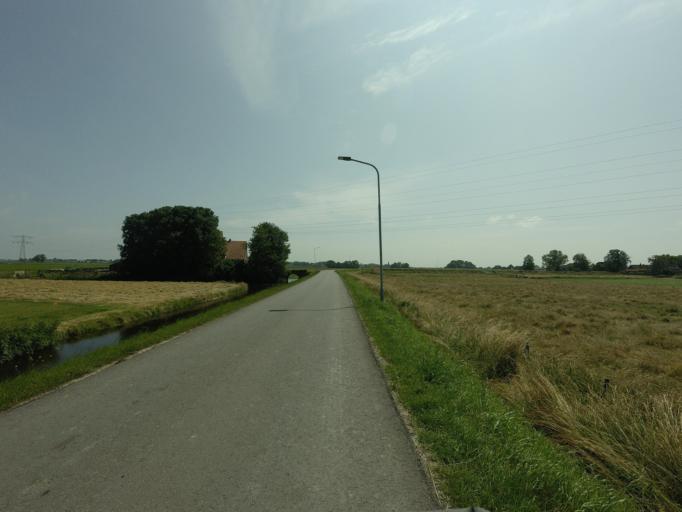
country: NL
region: North Holland
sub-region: Gemeente Heerhugowaard
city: Heerhugowaard
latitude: 52.6387
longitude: 4.8797
